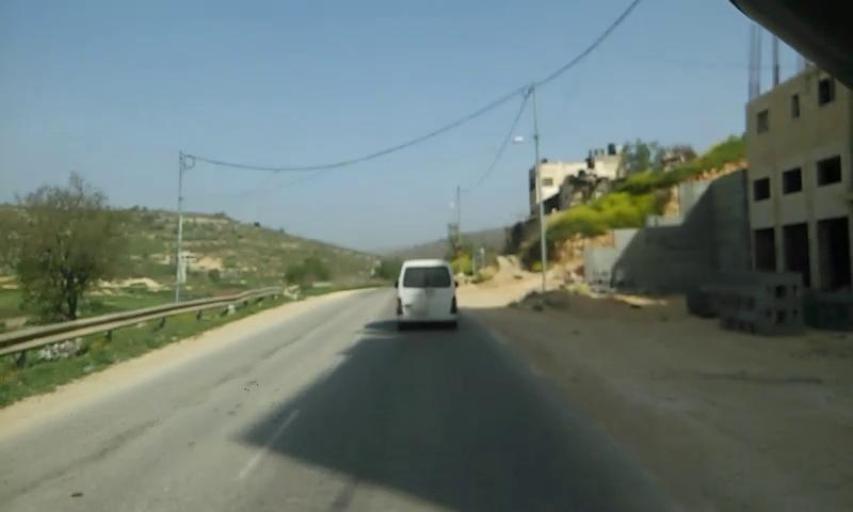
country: PS
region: West Bank
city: Dura al Qar`
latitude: 31.9730
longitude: 35.2346
